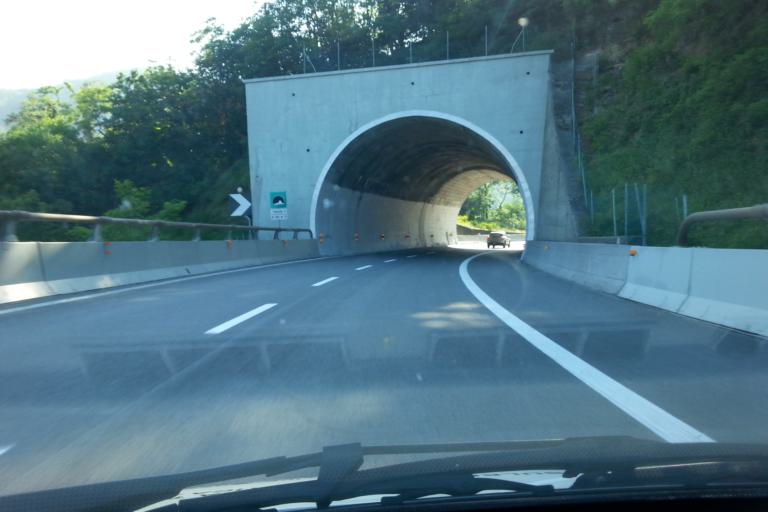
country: IT
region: Liguria
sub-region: Provincia di Savona
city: Quiliano
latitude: 44.3150
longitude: 8.3778
